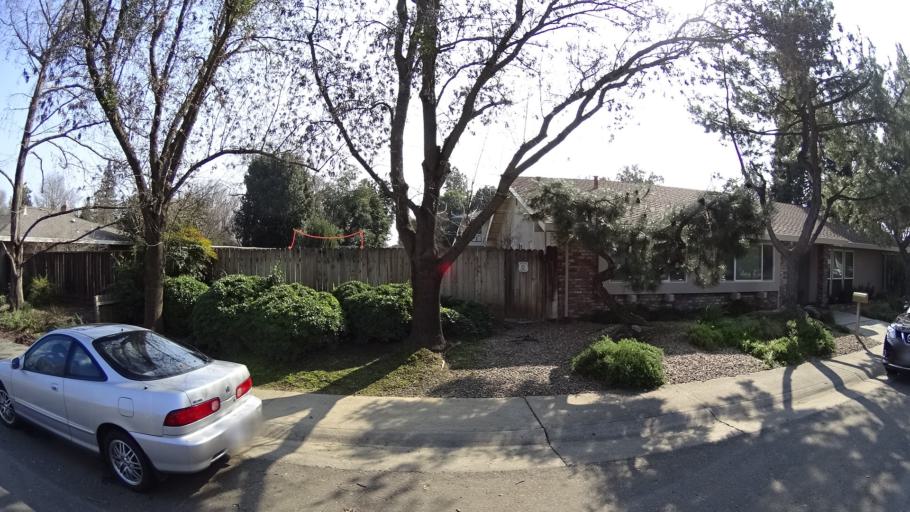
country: US
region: California
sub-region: Yolo County
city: Davis
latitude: 38.5483
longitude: -121.7775
